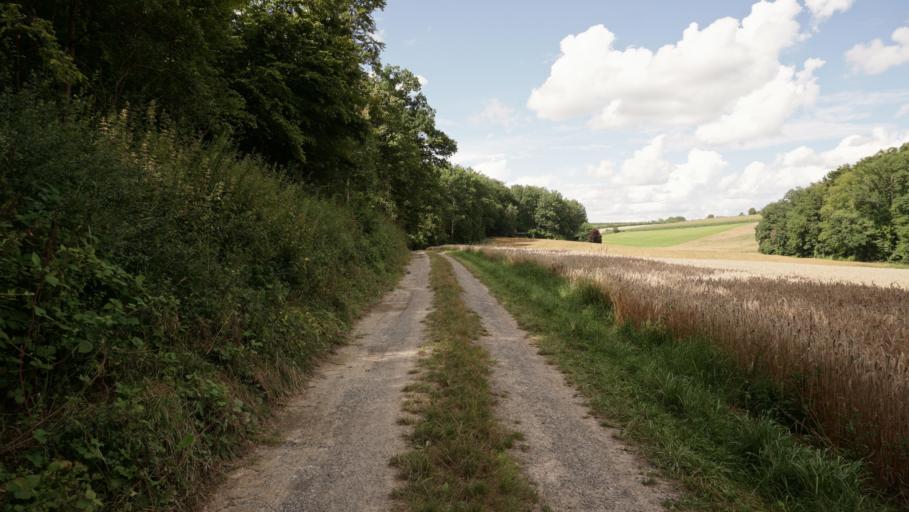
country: DE
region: Baden-Wuerttemberg
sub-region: Regierungsbezirk Stuttgart
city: Gundelsheim
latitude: 49.3133
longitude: 9.2089
